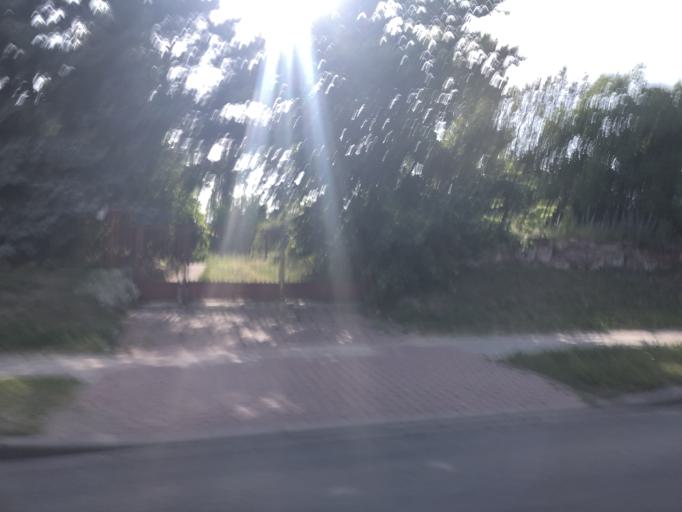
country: PL
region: Podlasie
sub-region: Lomza
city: Lomza
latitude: 53.1709
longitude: 22.0442
